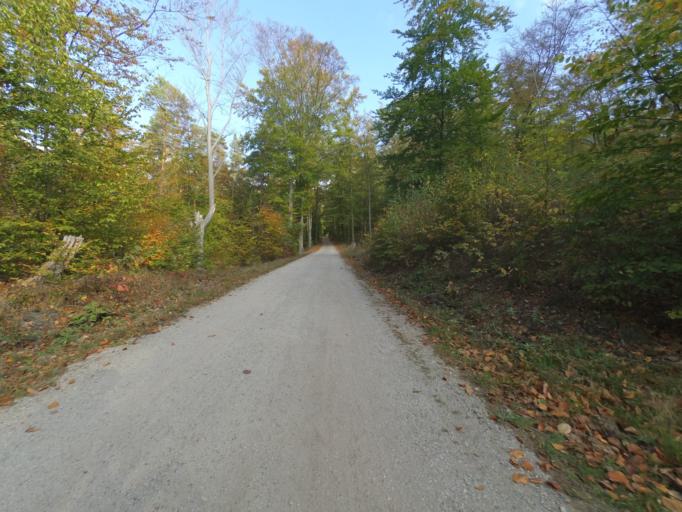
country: DE
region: Saxony
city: Albertstadt
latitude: 51.0937
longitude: 13.7957
